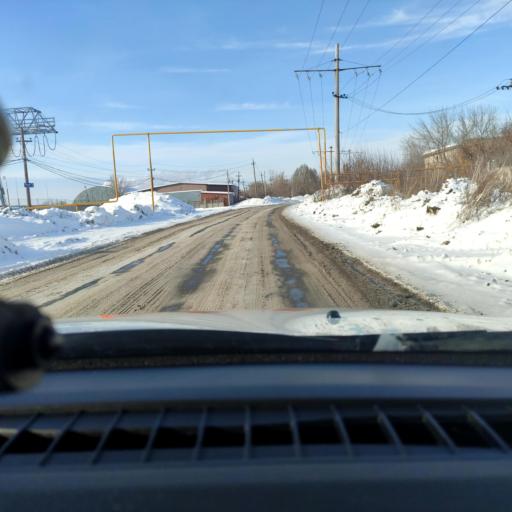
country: RU
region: Samara
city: Smyshlyayevka
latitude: 53.2571
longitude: 50.3663
